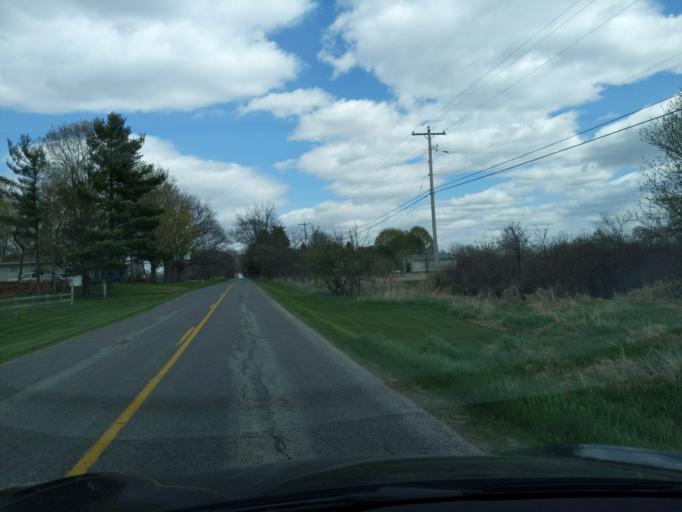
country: US
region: Michigan
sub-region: Ingham County
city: Holt
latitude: 42.6184
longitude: -84.5298
